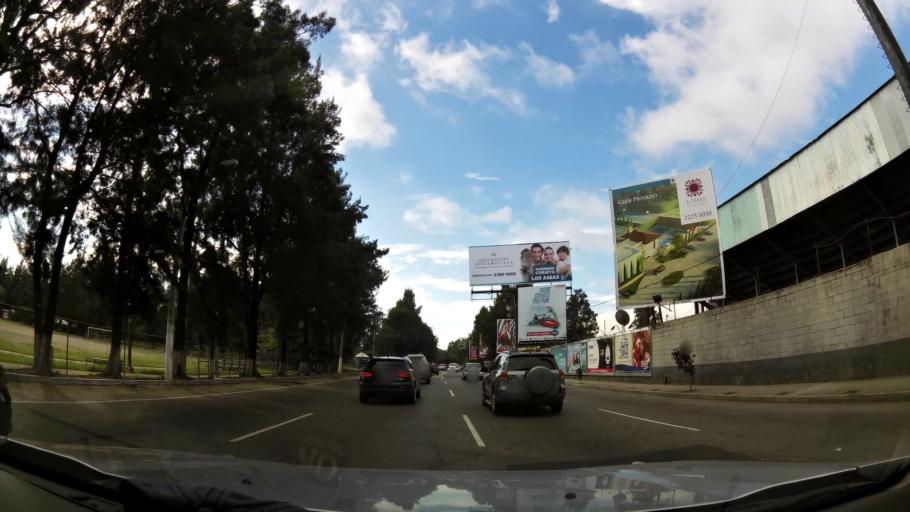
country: GT
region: Guatemala
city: Guatemala City
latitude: 14.6151
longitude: -90.5091
